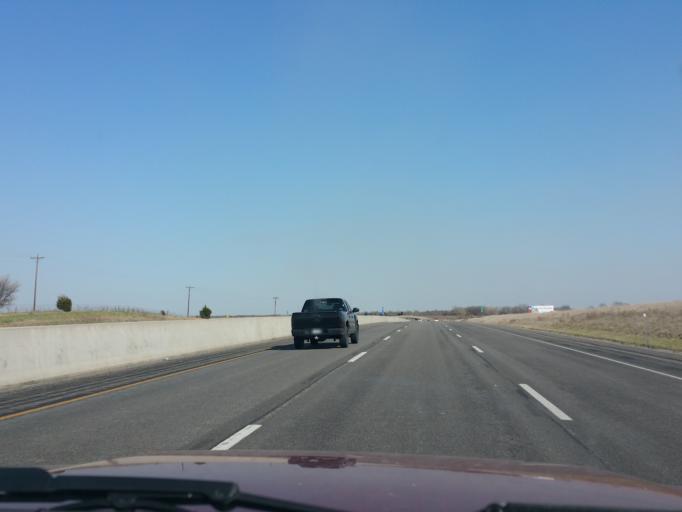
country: US
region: Kansas
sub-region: Douglas County
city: Lawrence
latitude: 39.0044
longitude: -95.4412
